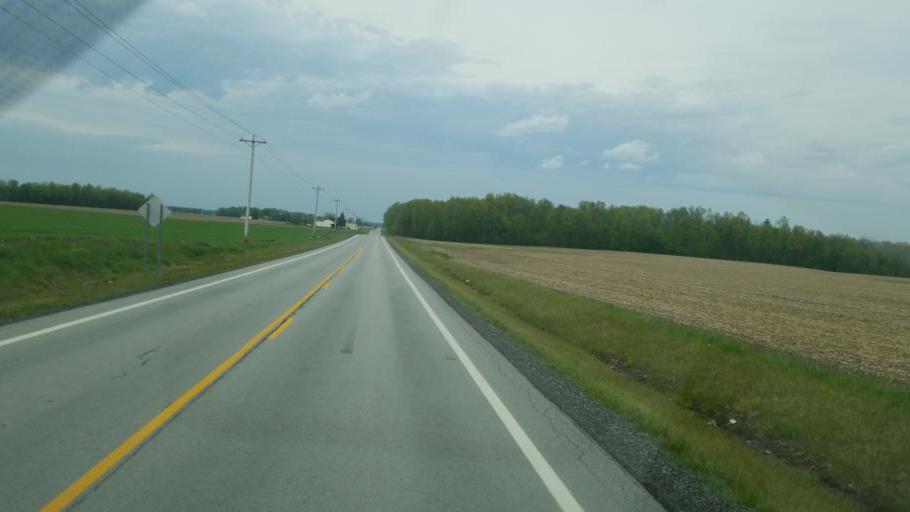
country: US
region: Ohio
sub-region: Huron County
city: Plymouth
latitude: 40.9640
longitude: -82.7433
